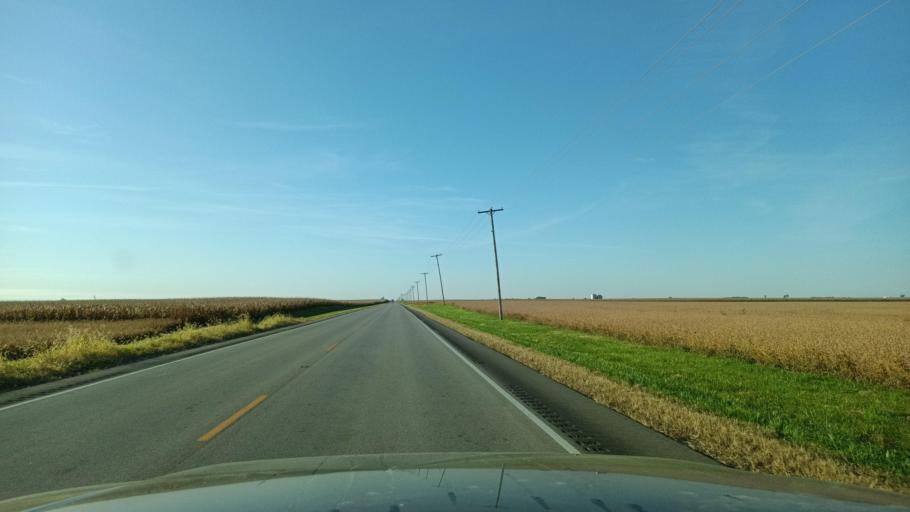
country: US
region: Illinois
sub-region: Douglas County
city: Villa Grove
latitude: 39.7859
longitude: -87.9397
